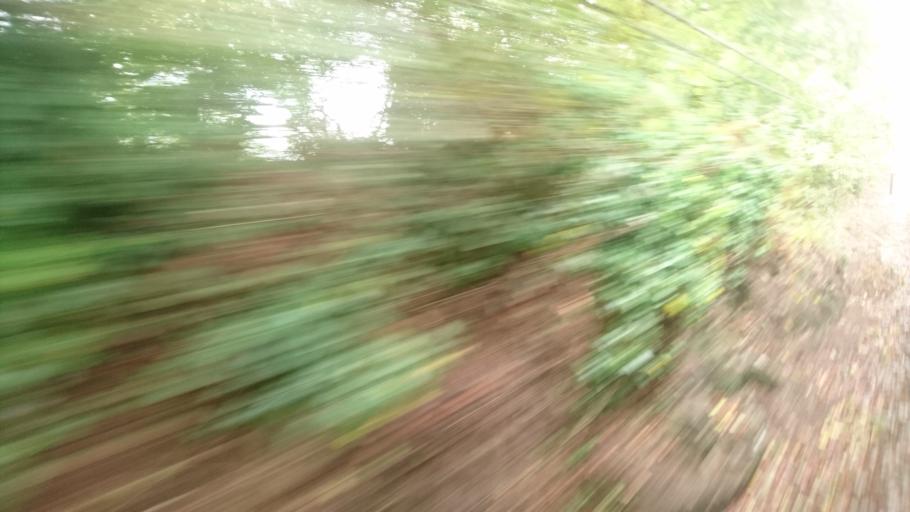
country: PT
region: Viseu
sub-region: Cinfaes
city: Cinfaes
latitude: 41.1018
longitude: -8.0838
